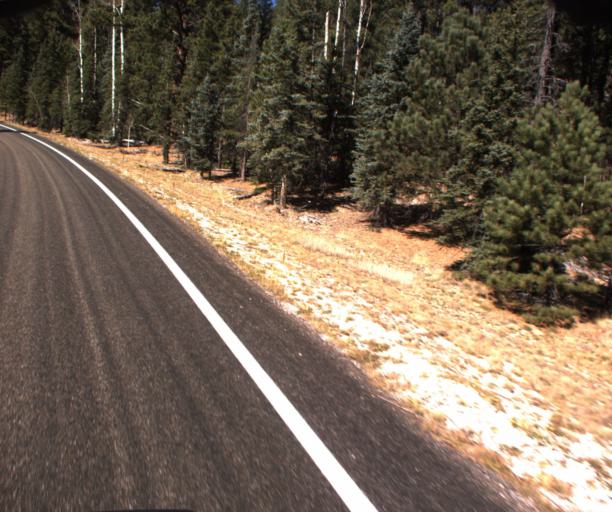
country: US
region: Arizona
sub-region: Coconino County
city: Grand Canyon
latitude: 36.5341
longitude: -112.1523
